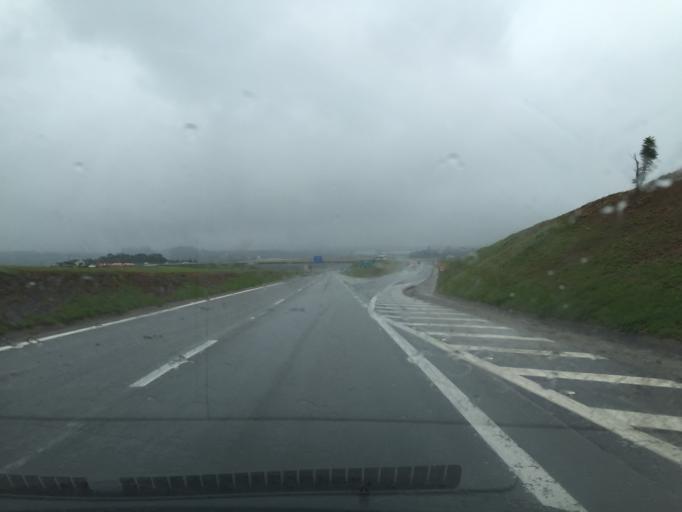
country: BR
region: Sao Paulo
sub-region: Itu
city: Itu
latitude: -23.4011
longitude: -47.3362
